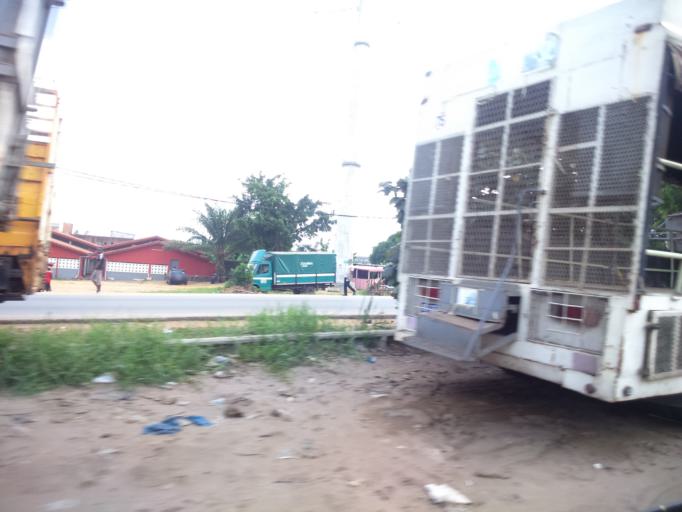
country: CI
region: Lagunes
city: Abidjan
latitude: 5.3597
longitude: -4.0851
